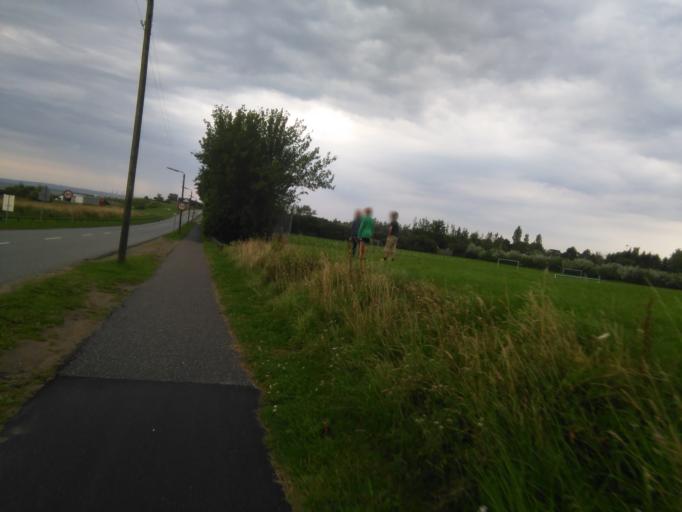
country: DK
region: Central Jutland
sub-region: Arhus Kommune
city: Hjortshoj
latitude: 56.2248
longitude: 10.3026
